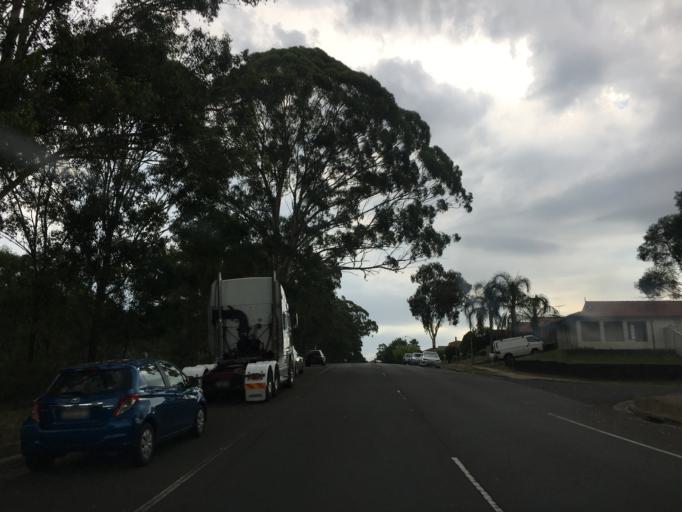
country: AU
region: New South Wales
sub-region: Liverpool
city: Miller
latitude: -33.9108
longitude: 150.8695
